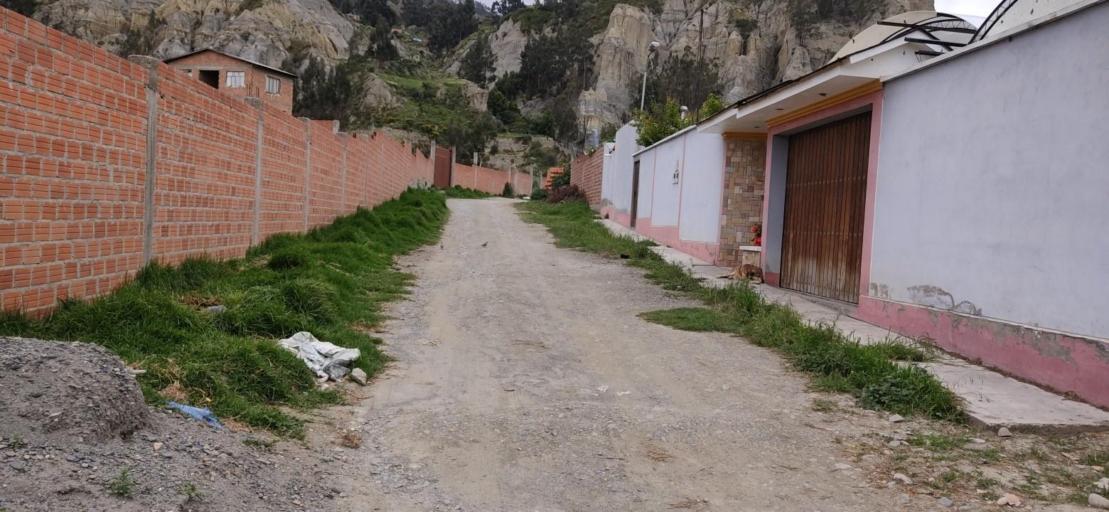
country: BO
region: La Paz
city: La Paz
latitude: -16.4977
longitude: -68.0877
